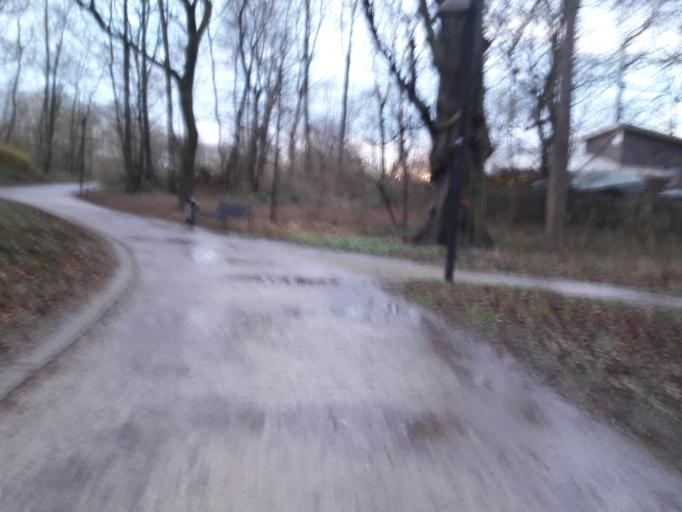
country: DE
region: North Rhine-Westphalia
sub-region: Regierungsbezirk Detmold
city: Paderborn
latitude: 51.7477
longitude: 8.7089
